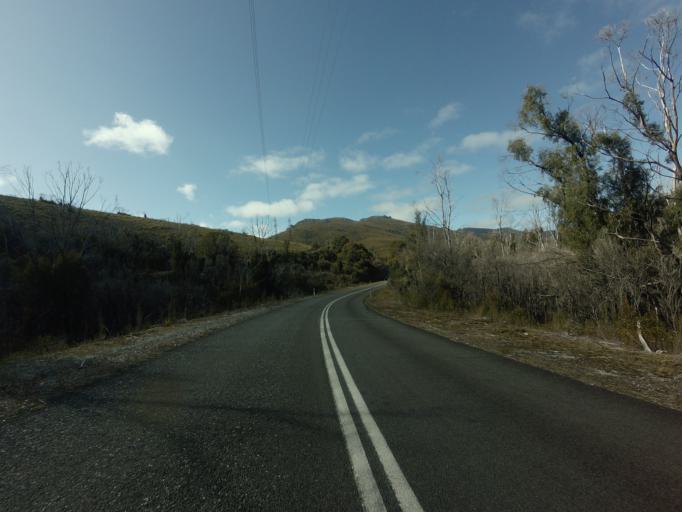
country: AU
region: Tasmania
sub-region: Huon Valley
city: Geeveston
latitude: -42.8480
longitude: 146.1737
